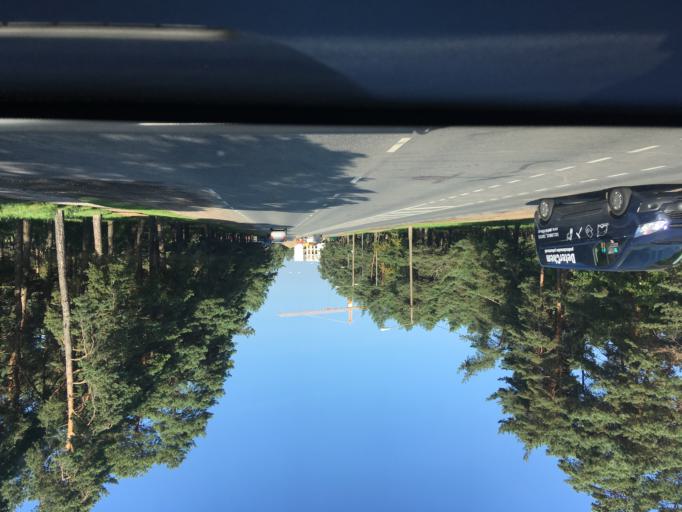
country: EE
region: Harju
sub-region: Saue vald
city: Laagri
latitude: 59.4071
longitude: 24.6676
